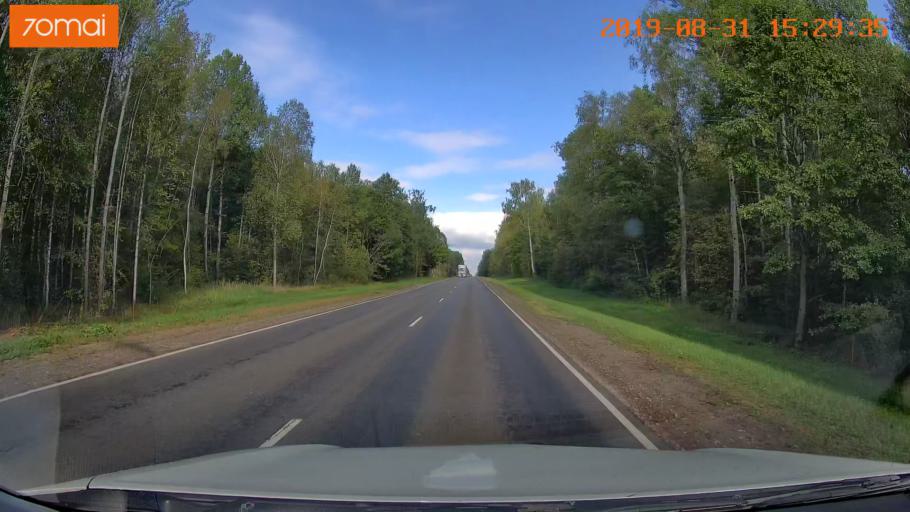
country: RU
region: Kaluga
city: Baryatino
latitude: 54.5699
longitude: 34.6092
